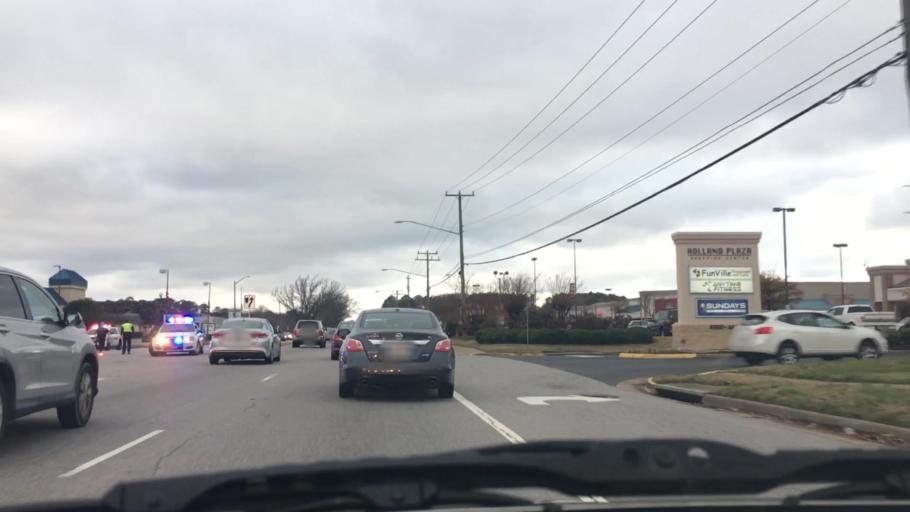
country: US
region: Virginia
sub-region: City of Virginia Beach
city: Virginia Beach
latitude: 36.8203
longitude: -76.1215
